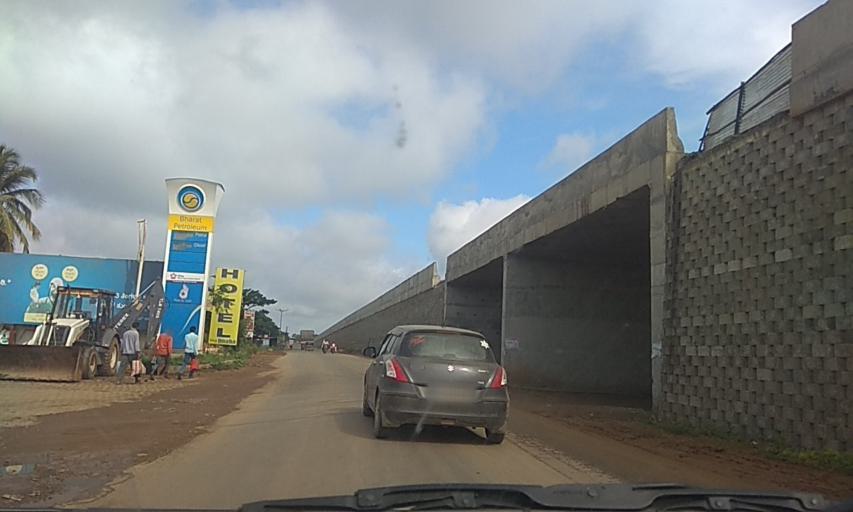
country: IN
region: Karnataka
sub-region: Haveri
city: Shiggaon
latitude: 14.9931
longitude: 75.2150
